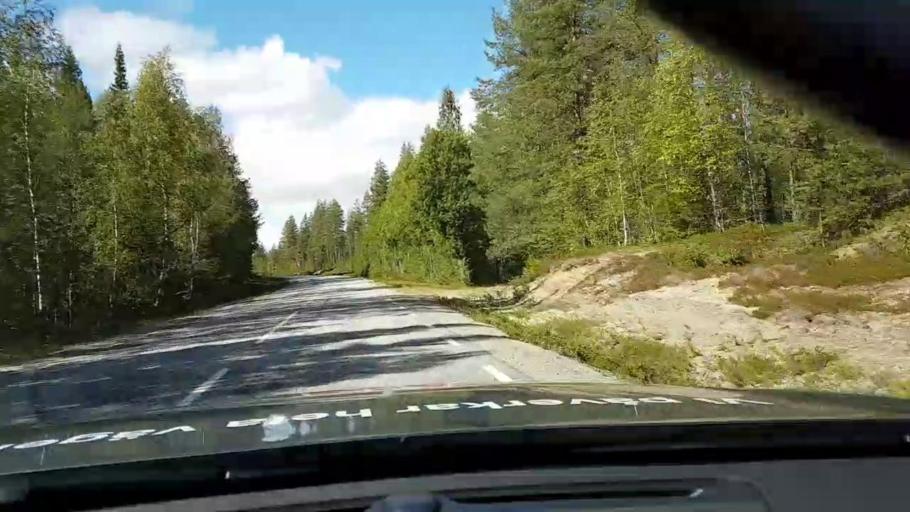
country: SE
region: Vaesternorrland
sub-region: OErnskoeldsviks Kommun
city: Bredbyn
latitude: 63.6606
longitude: 17.8525
